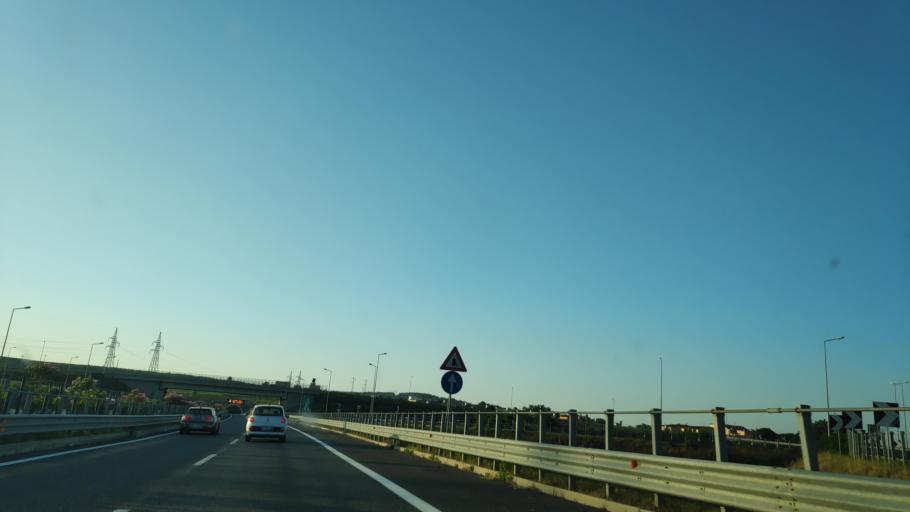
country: IT
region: Calabria
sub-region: Provincia di Reggio Calabria
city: Ceramida-Pellegrina
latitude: 38.3100
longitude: 15.8442
